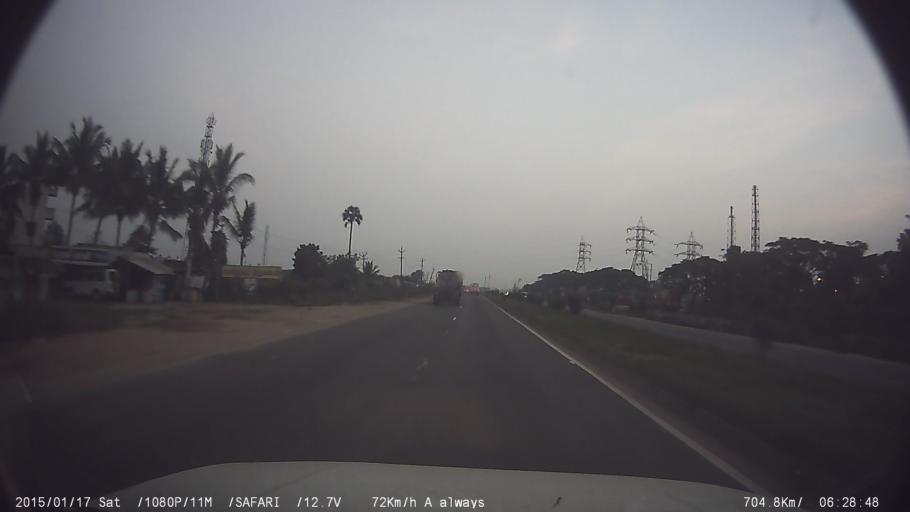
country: IN
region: Tamil Nadu
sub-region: Kancheepuram
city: Sriperumbudur
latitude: 12.9371
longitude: 79.9124
